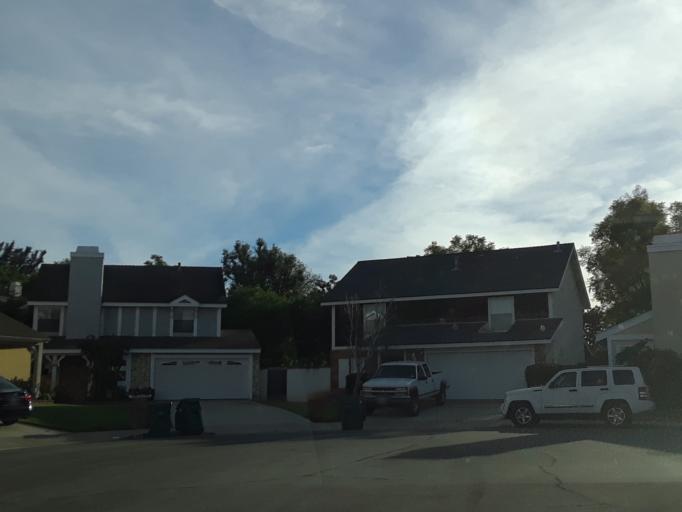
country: US
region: California
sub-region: Orange County
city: North Tustin
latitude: 33.7164
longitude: -117.7624
